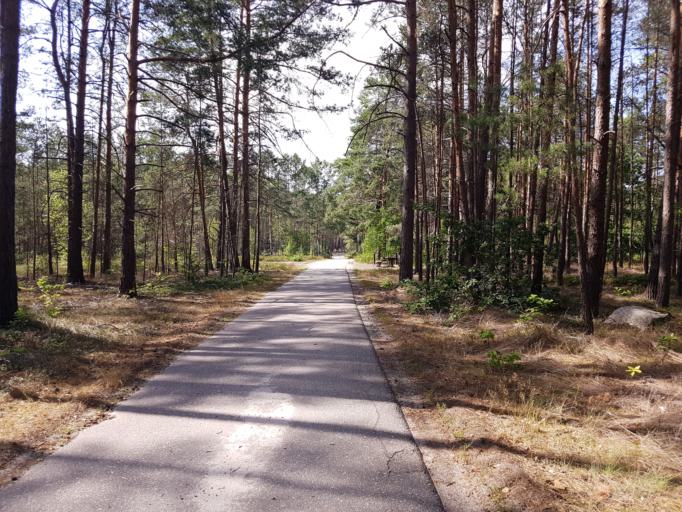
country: DE
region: Brandenburg
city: Finsterwalde
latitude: 51.6233
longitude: 13.6669
